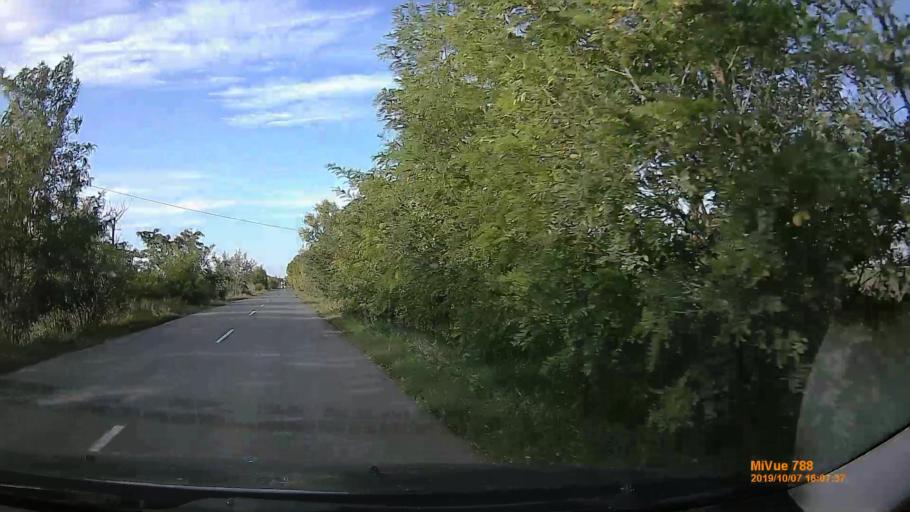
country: HU
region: Bekes
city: Szarvas
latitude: 46.8029
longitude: 20.6197
